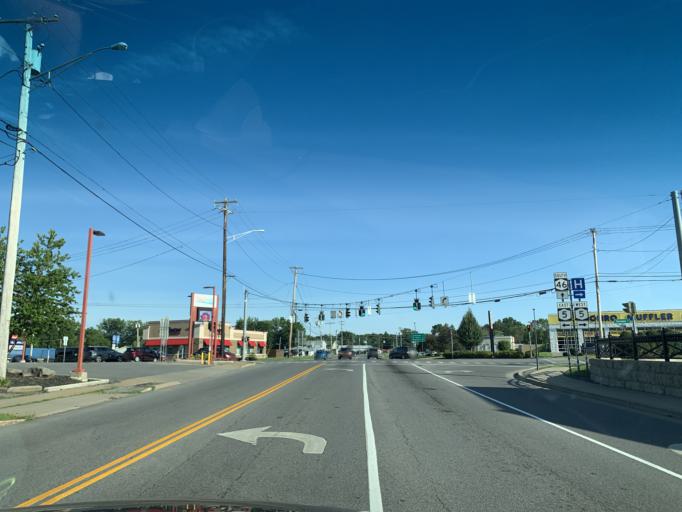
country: US
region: New York
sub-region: Madison County
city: Oneida
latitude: 43.0794
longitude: -75.6424
